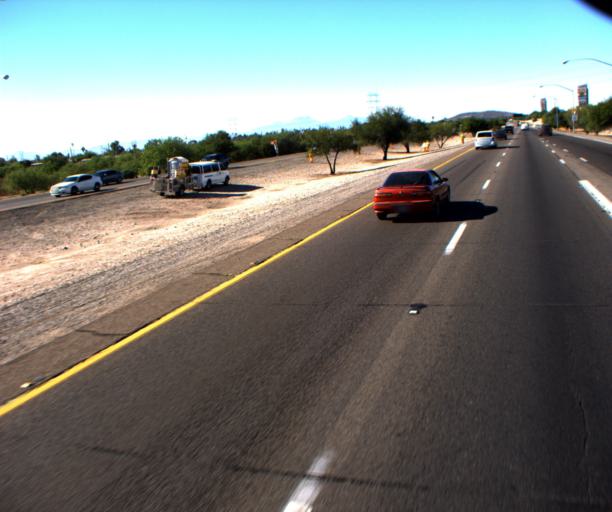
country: US
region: Arizona
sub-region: Pima County
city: South Tucson
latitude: 32.1587
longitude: -110.9862
